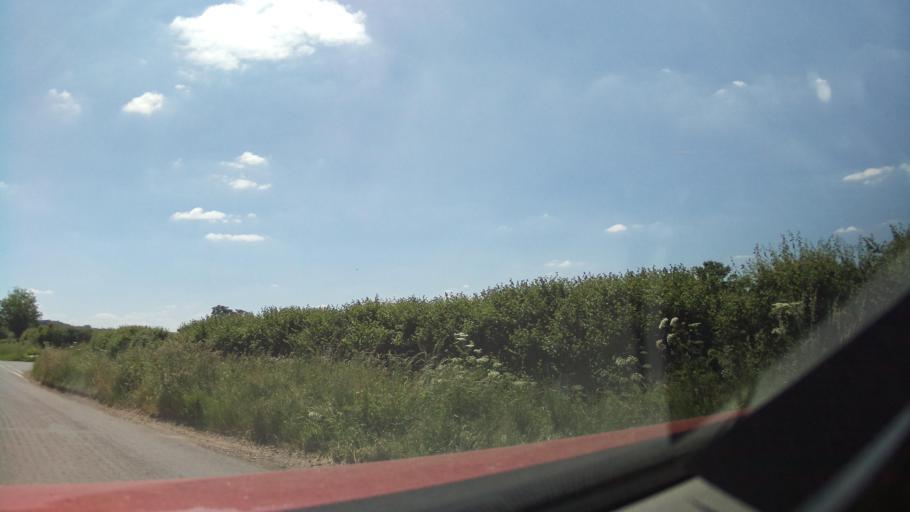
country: GB
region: England
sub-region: Wiltshire
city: Bremhill
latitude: 51.4887
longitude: -2.0436
